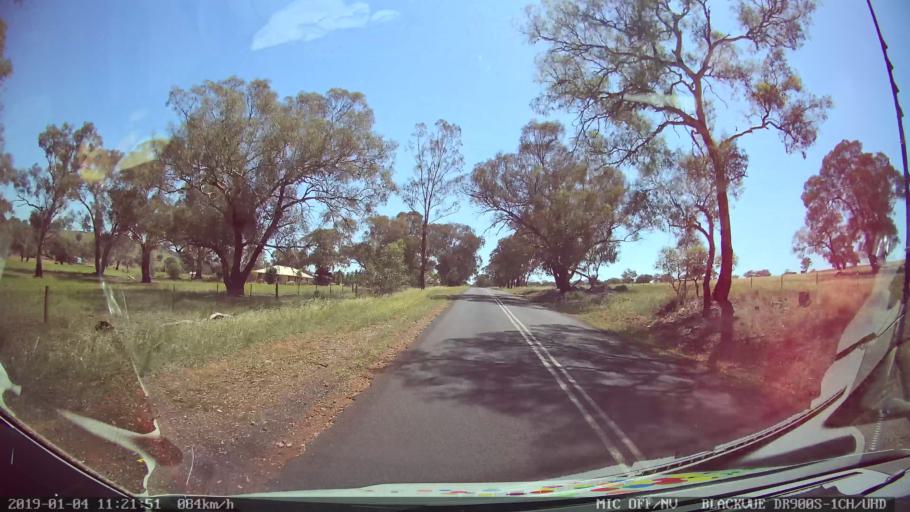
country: AU
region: New South Wales
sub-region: Cabonne
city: Molong
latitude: -33.1512
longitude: 148.7157
